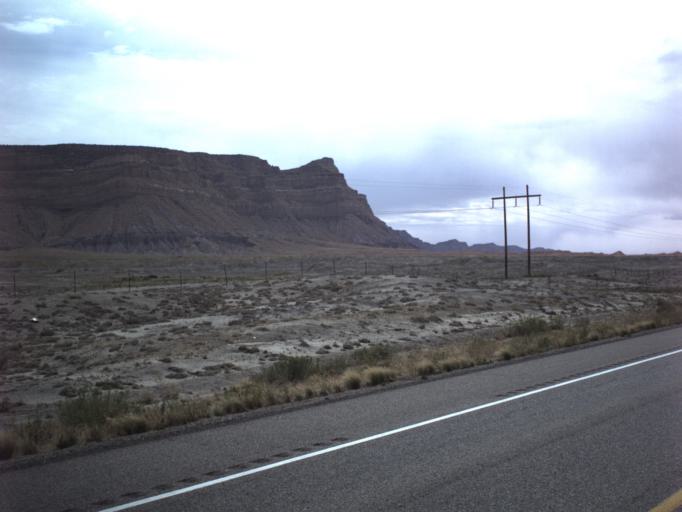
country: US
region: Utah
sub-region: Carbon County
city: East Carbon City
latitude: 39.2203
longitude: -110.3387
